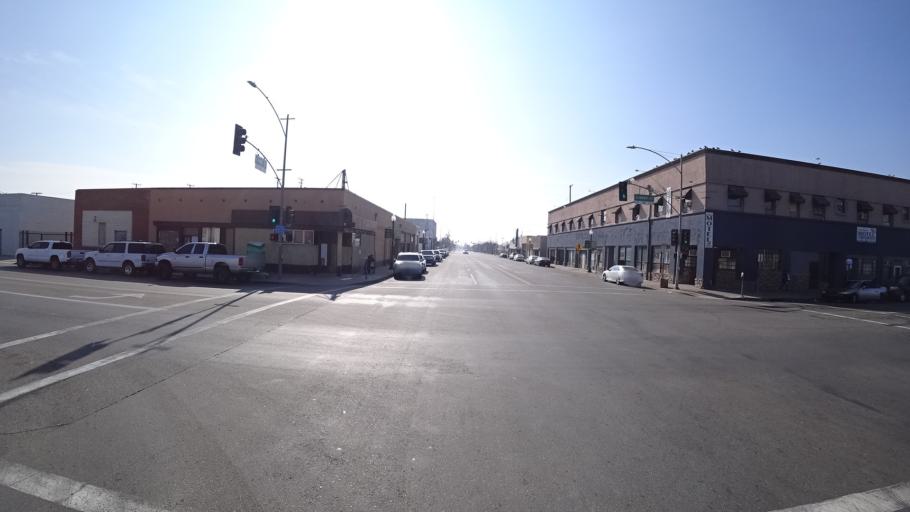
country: US
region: California
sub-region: Kern County
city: Bakersfield
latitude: 35.3770
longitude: -118.9928
